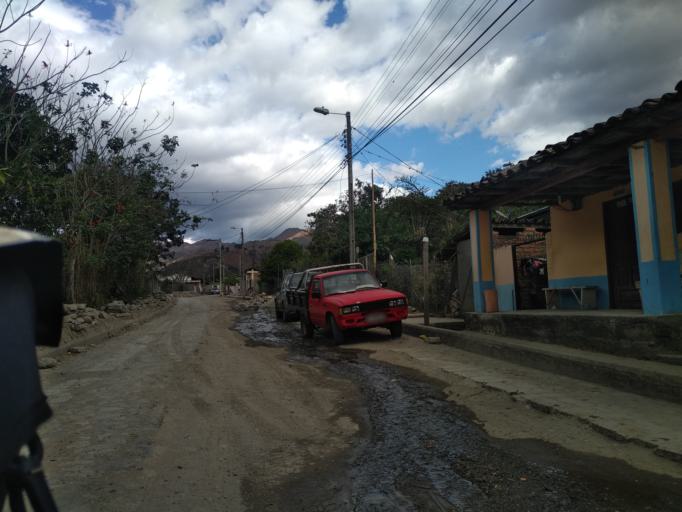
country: EC
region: Loja
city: Loja
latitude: -4.2560
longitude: -79.2223
